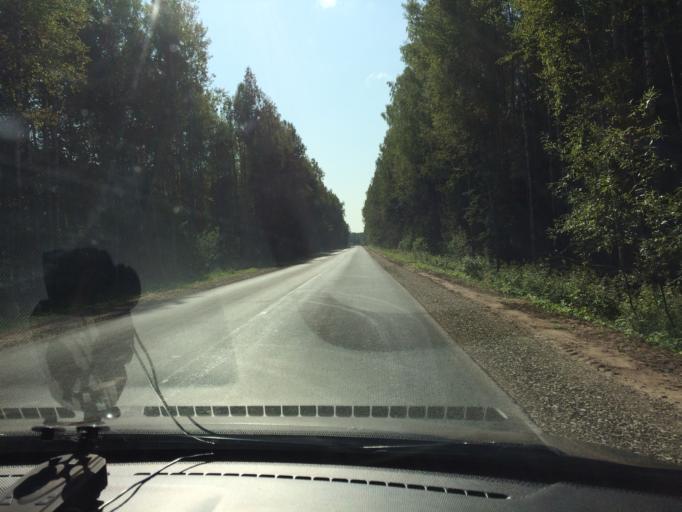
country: RU
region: Mariy-El
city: Surok
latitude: 56.5597
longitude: 48.3070
